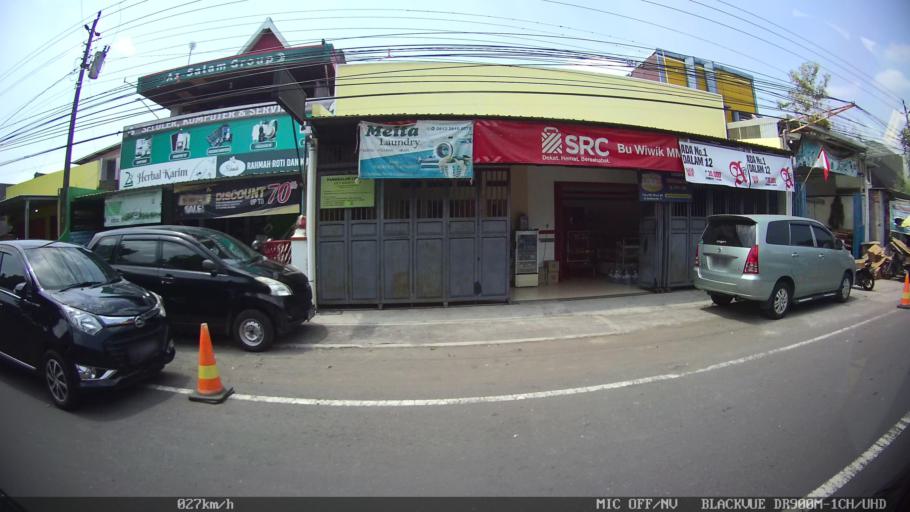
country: ID
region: Daerah Istimewa Yogyakarta
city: Yogyakarta
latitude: -7.8151
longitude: 110.3916
